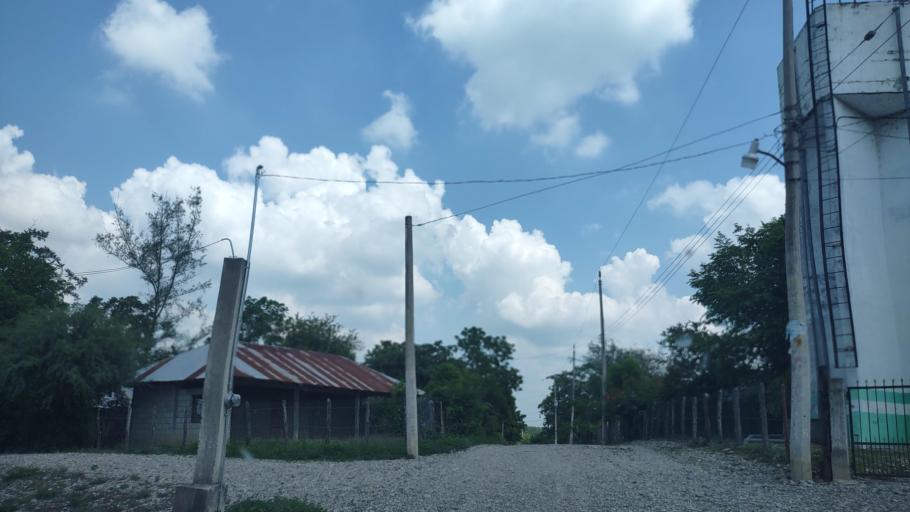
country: MX
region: Veracruz
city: Tempoal de Sanchez
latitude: 21.5479
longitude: -98.2753
